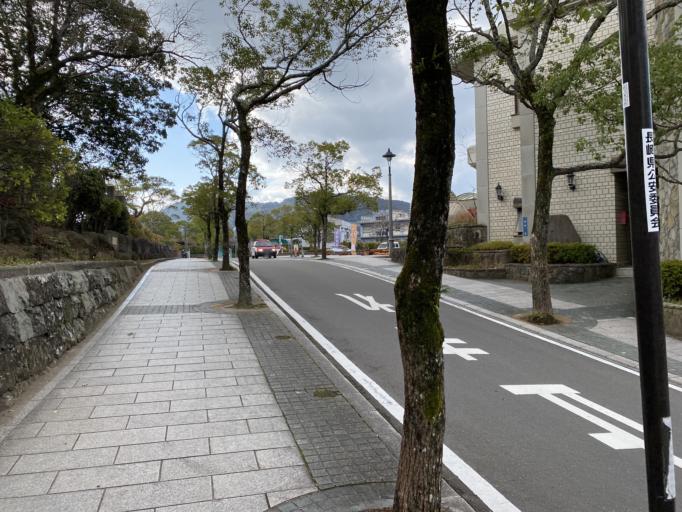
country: JP
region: Nagasaki
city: Nagasaki-shi
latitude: 32.7772
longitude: 129.8637
